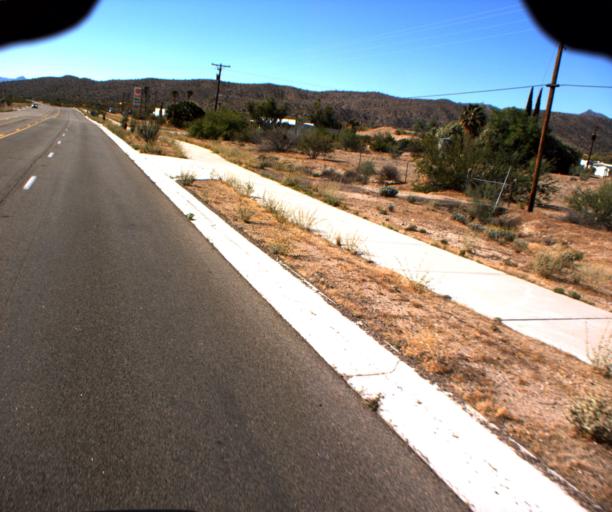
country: US
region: Arizona
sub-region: Yavapai County
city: Bagdad
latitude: 34.7024
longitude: -113.6109
